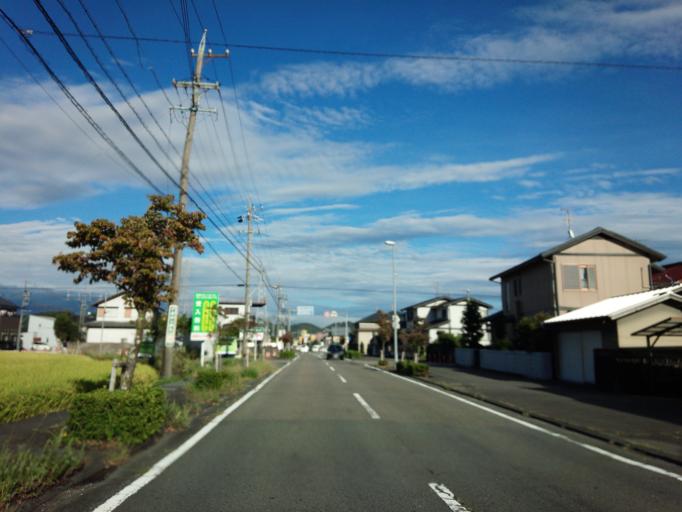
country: JP
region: Shizuoka
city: Shimada
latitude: 34.8416
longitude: 138.1582
